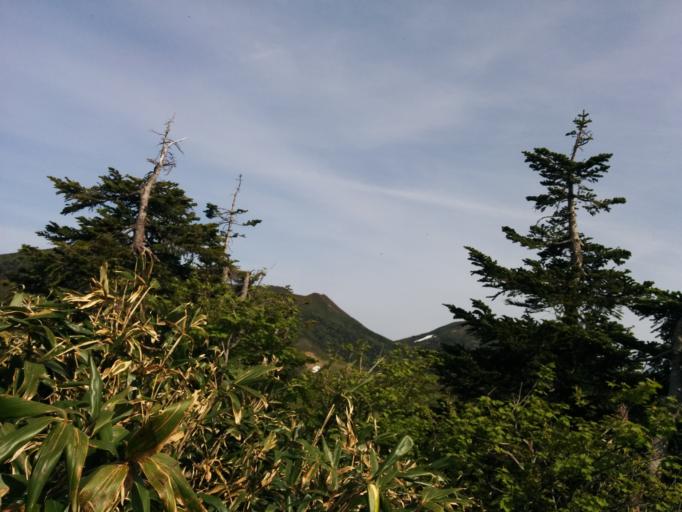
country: JP
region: Aomori
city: Aomori Shi
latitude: 40.6751
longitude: 140.8624
